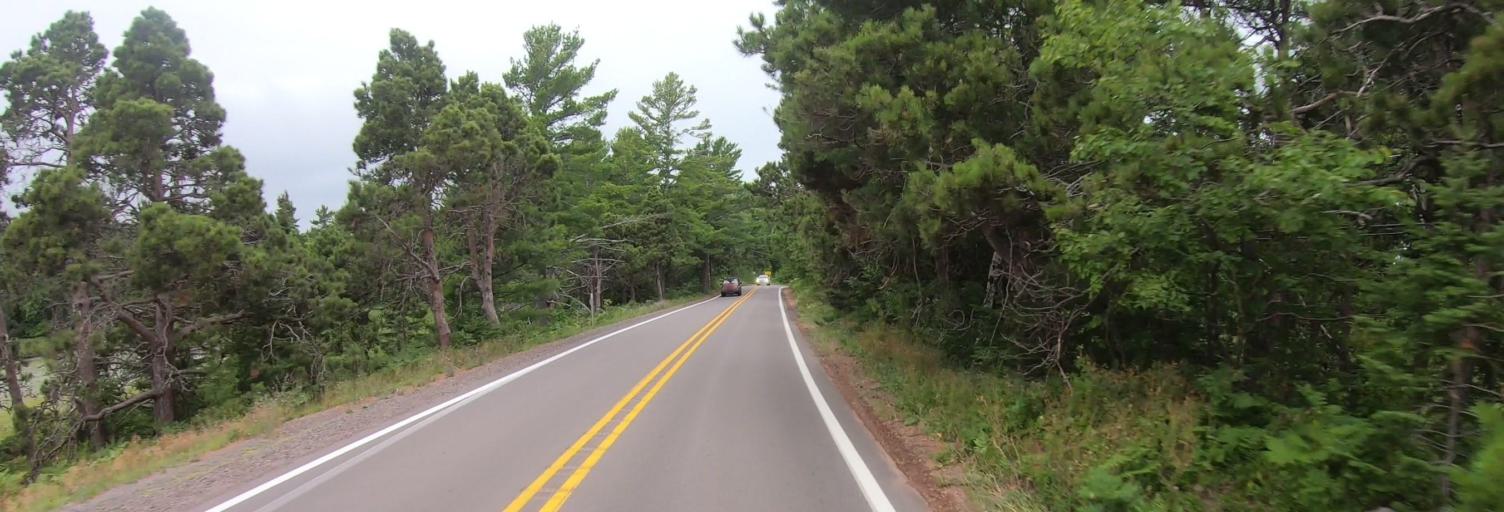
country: US
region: Michigan
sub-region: Keweenaw County
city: Eagle River
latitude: 47.4587
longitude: -88.1234
